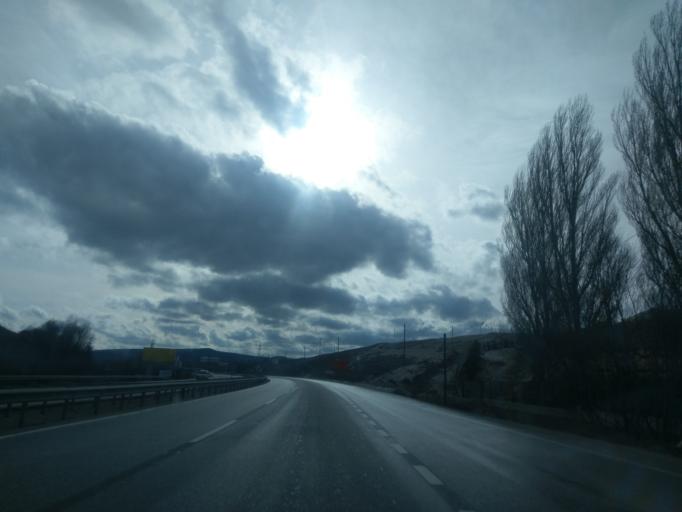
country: TR
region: Eskisehir
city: Inonu
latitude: 39.7069
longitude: 30.1560
